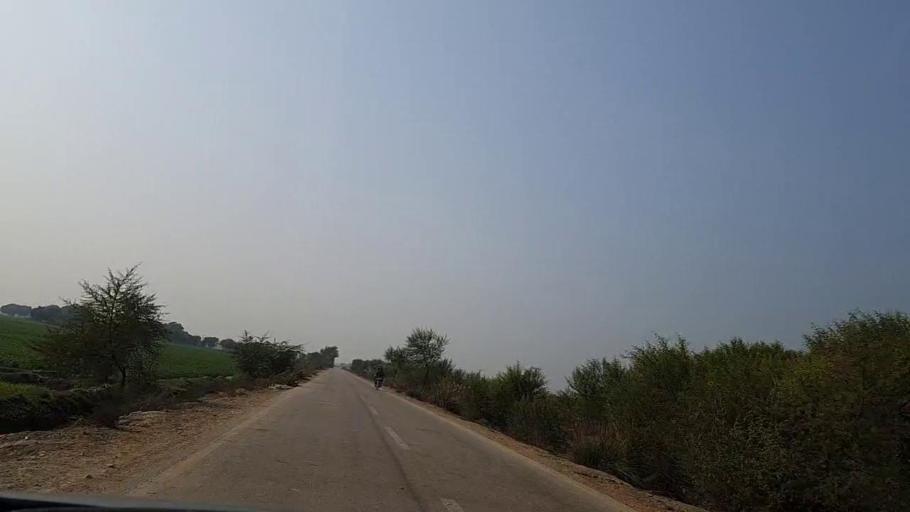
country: PK
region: Sindh
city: Sann
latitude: 26.1391
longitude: 68.1669
